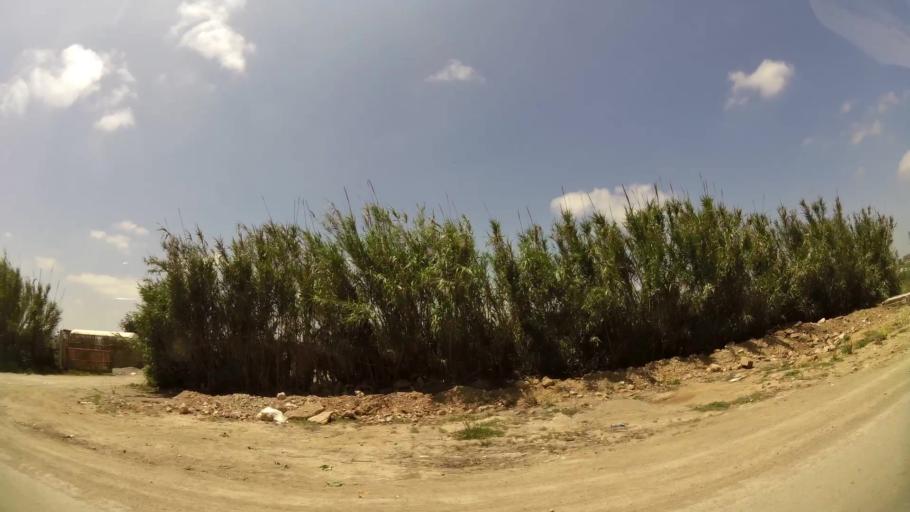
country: MA
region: Fes-Boulemane
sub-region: Fes
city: Fes
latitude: 34.0398
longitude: -5.0611
